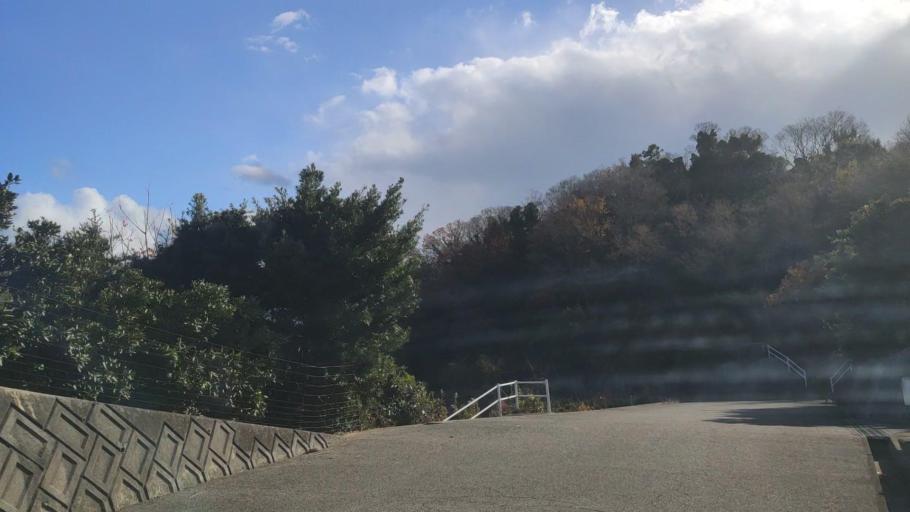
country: JP
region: Hiroshima
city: Innoshima
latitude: 34.2148
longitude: 133.1269
